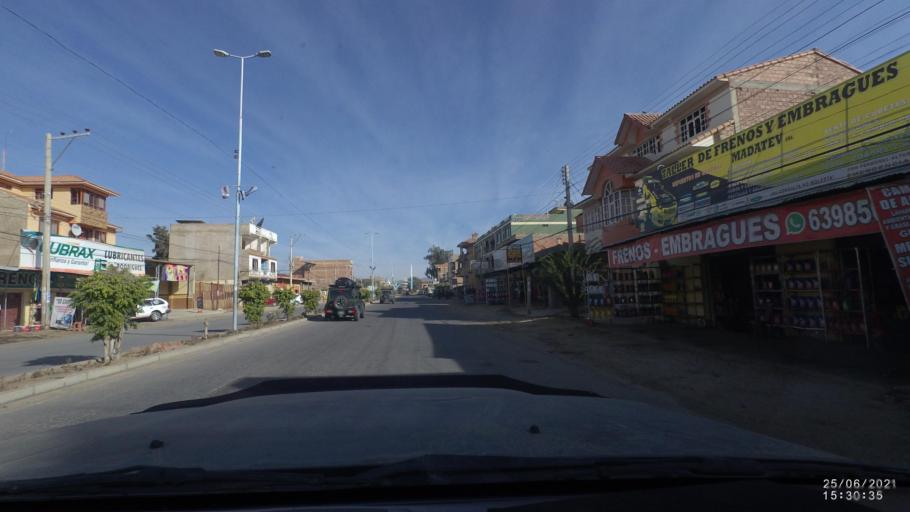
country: BO
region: Cochabamba
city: Cliza
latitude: -17.5859
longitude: -65.9338
